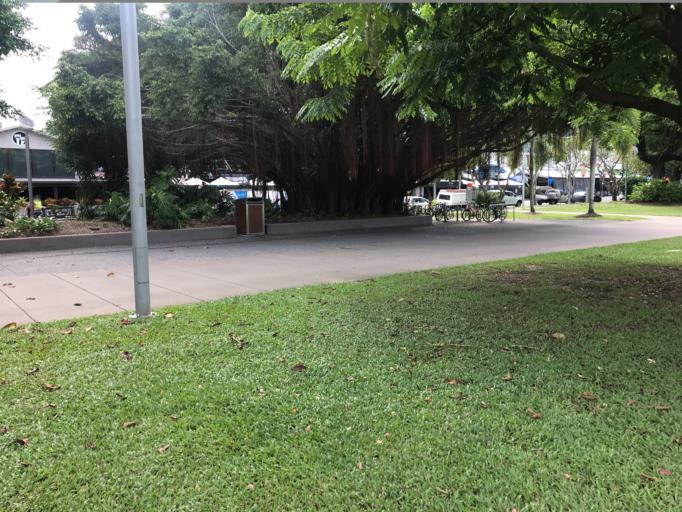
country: AU
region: Queensland
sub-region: Cairns
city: Cairns
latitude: -16.9200
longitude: 145.7778
